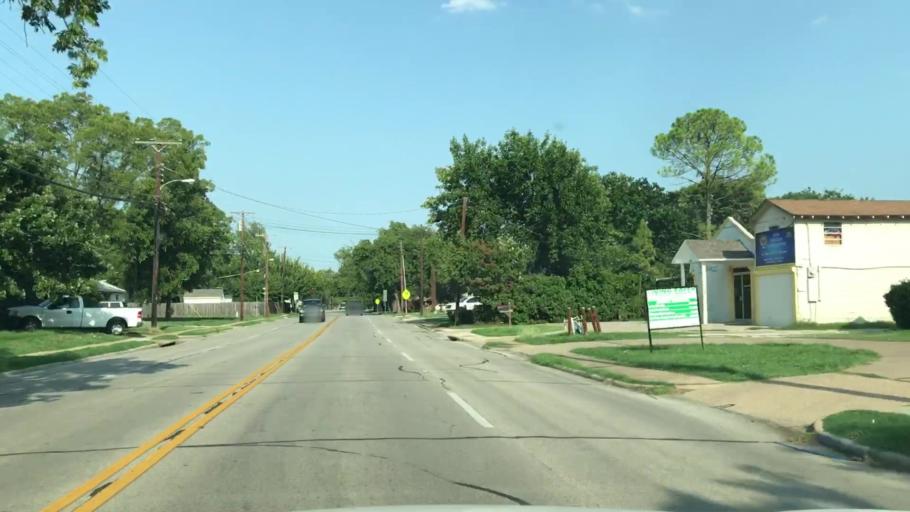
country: US
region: Texas
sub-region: Dallas County
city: Irving
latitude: 32.8221
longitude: -96.9404
